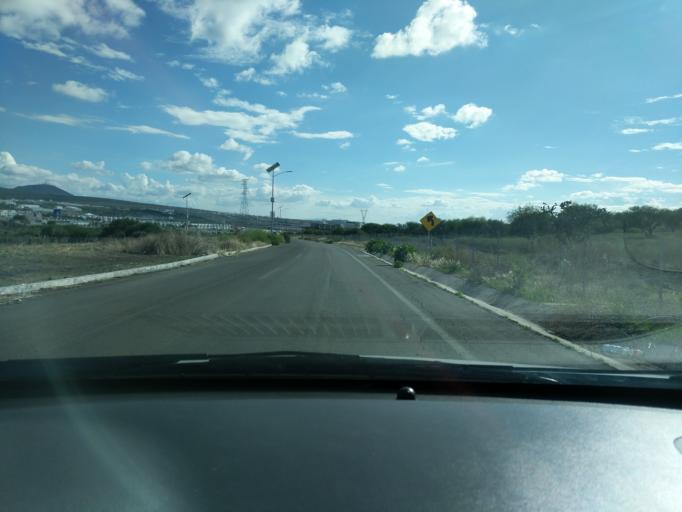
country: MX
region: Queretaro
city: La Canada
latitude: 20.5951
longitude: -100.3186
